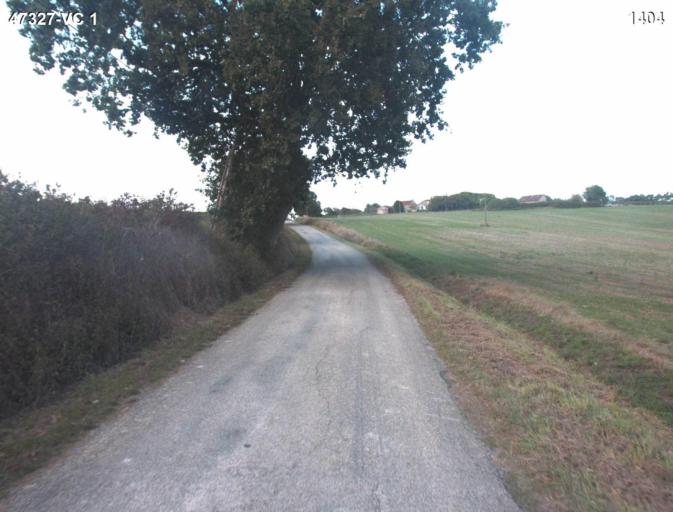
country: FR
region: Aquitaine
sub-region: Departement du Lot-et-Garonne
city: Barbaste
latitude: 44.1971
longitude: 0.2574
